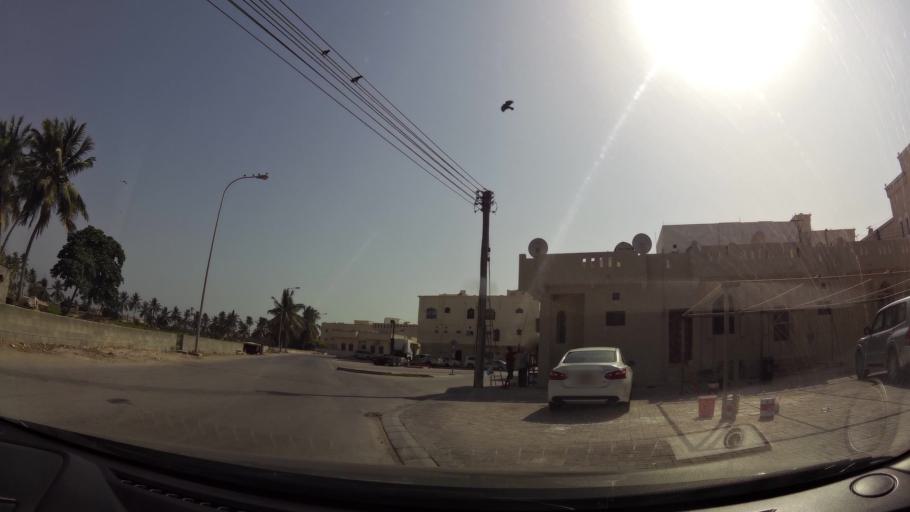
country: OM
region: Zufar
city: Salalah
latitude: 17.0028
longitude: 54.0522
